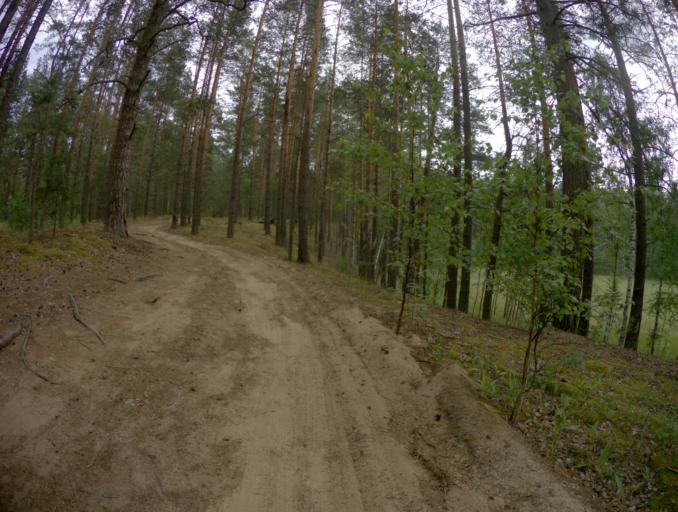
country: RU
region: Nizjnij Novgorod
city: Frolishchi
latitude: 56.3528
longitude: 42.7605
